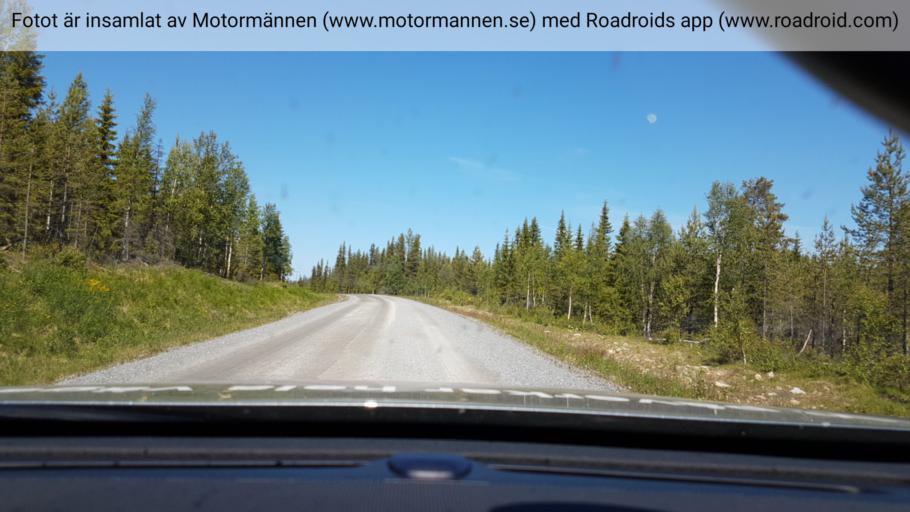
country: SE
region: Vaesterbotten
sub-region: Vilhelmina Kommun
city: Sjoberg
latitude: 64.6753
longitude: 15.7564
